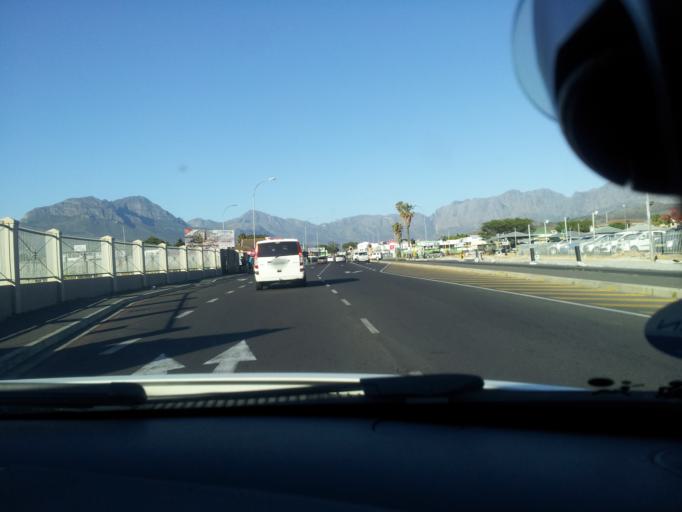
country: ZA
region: Western Cape
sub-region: Cape Winelands District Municipality
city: Stellenbosch
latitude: -34.1085
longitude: 18.8376
